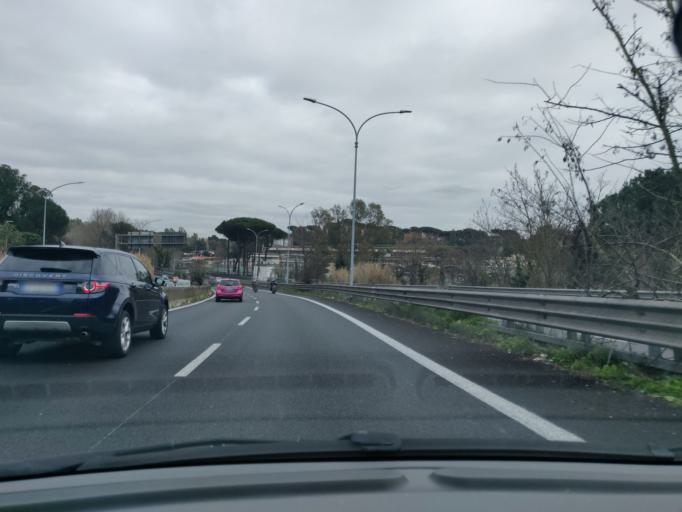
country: IT
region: Latium
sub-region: Citta metropolitana di Roma Capitale
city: La Massimina-Casal Lumbroso
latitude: 41.8845
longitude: 12.3915
